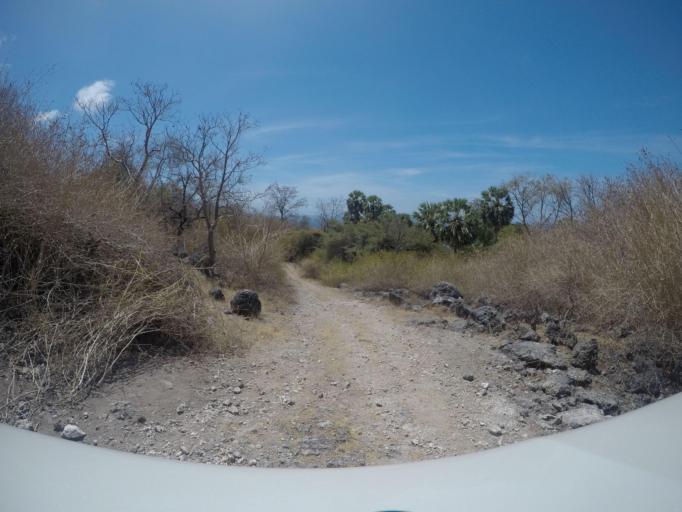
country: TL
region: Baucau
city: Baucau
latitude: -8.4429
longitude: 126.4409
